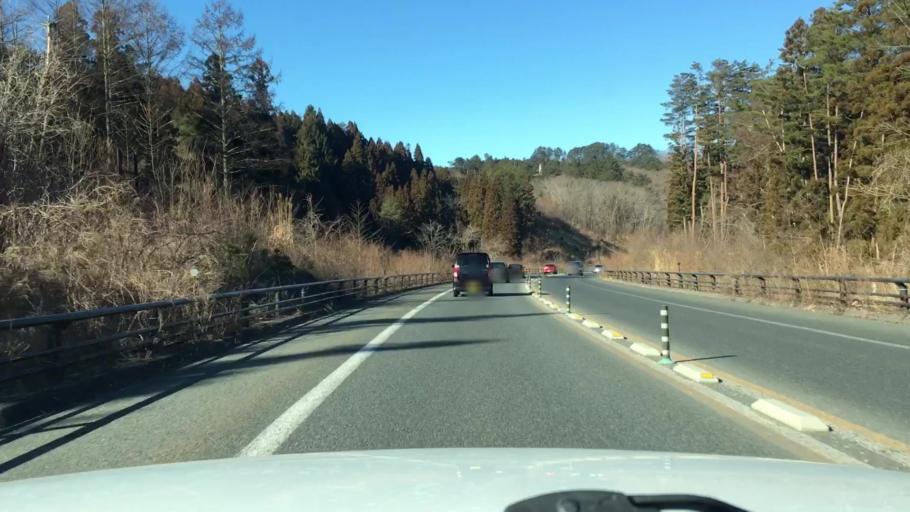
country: JP
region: Iwate
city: Miyako
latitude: 39.6034
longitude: 141.9320
